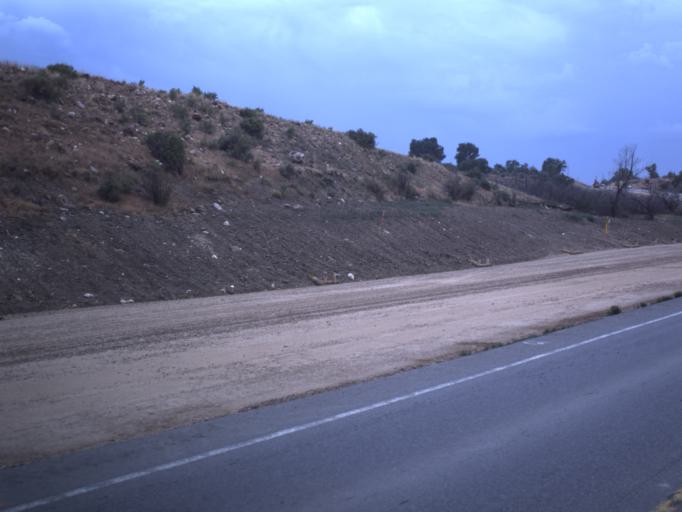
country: US
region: Utah
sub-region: Duchesne County
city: Roosevelt
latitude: 40.2548
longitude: -110.0658
